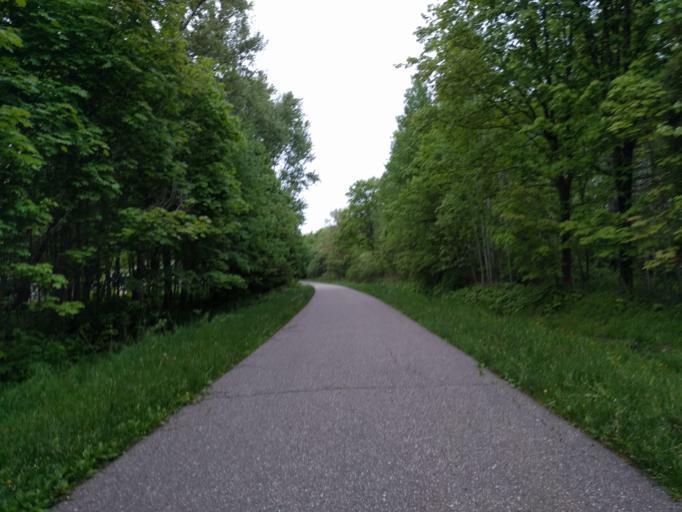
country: US
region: Michigan
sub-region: Marquette County
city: Trowbridge Park
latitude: 46.5520
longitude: -87.4172
